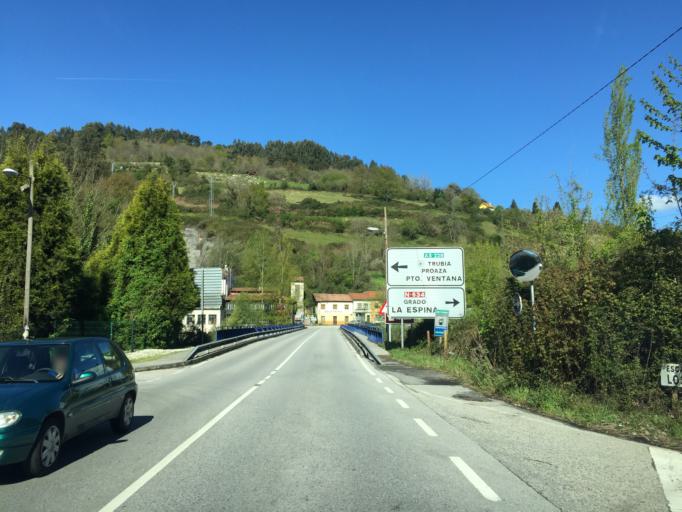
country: ES
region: Asturias
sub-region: Province of Asturias
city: Castandiello
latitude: 43.3534
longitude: -5.9648
